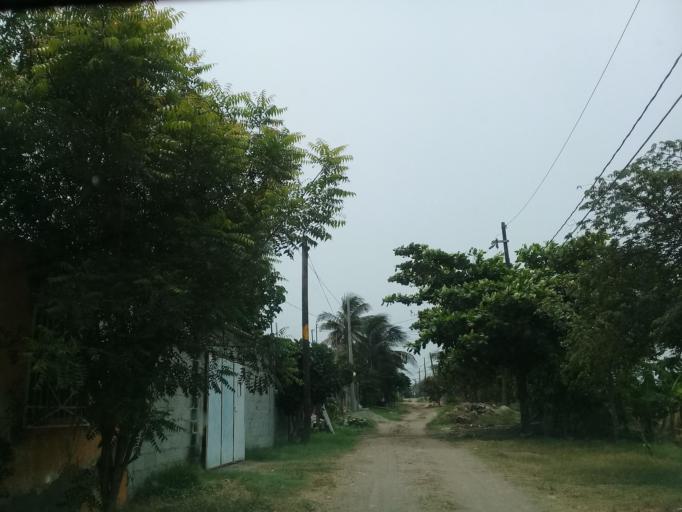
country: MX
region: Veracruz
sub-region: Veracruz
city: Las Amapolas
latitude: 19.1502
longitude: -96.2025
